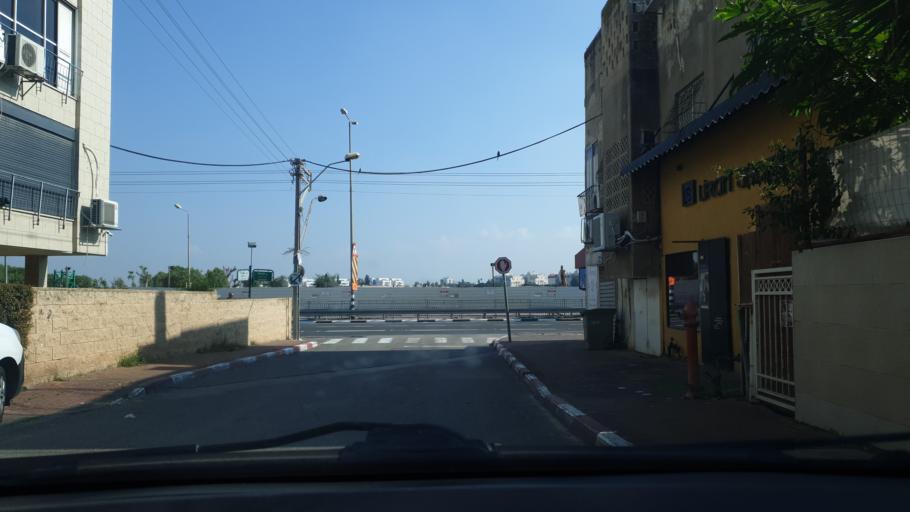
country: IL
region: Central District
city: Ramla
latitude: 31.9387
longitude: 34.8654
